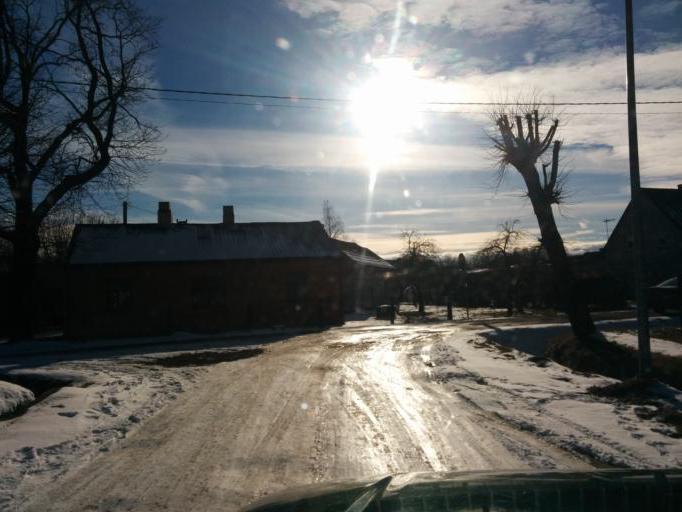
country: LV
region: Jelgava
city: Jelgava
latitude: 56.6547
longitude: 23.7033
